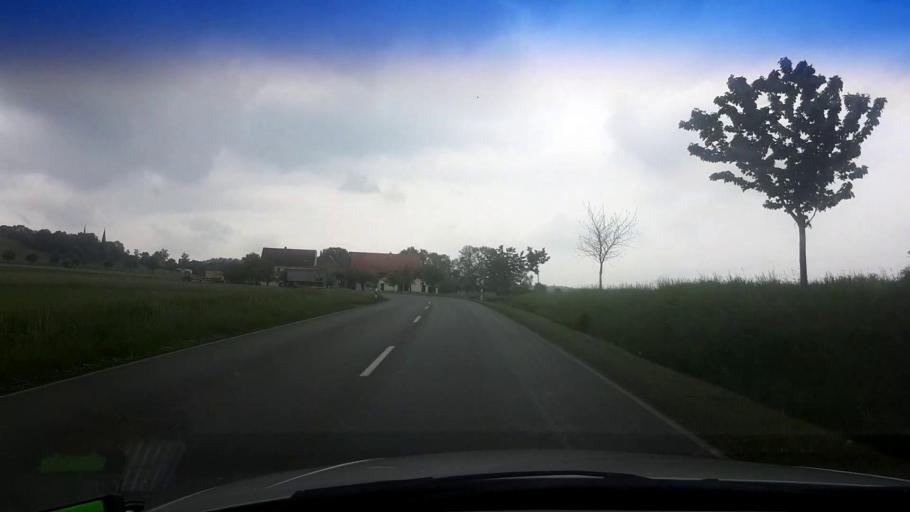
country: DE
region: Bavaria
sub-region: Upper Franconia
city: Goldkronach
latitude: 50.0020
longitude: 11.6807
